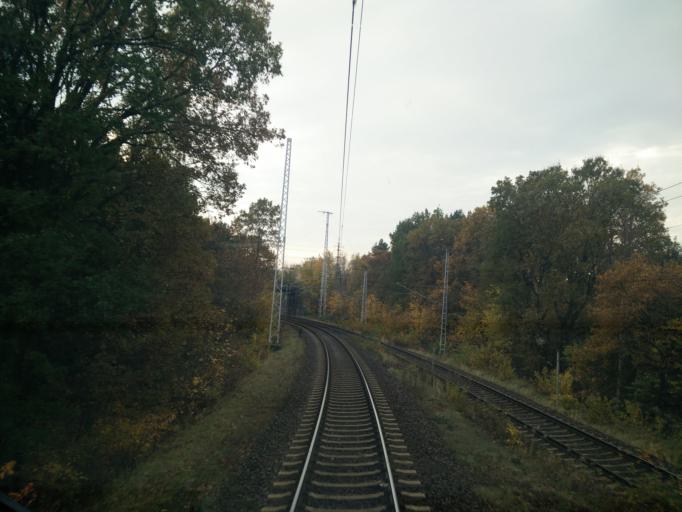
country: DE
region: Berlin
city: Adlershof
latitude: 52.4208
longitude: 13.5571
